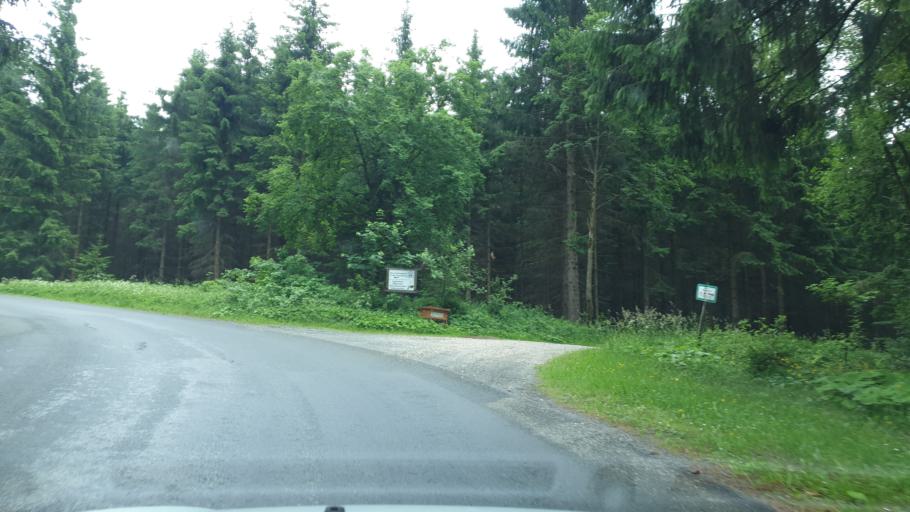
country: DE
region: Saxony
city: Tannenbergsthal
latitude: 50.4185
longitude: 12.4475
